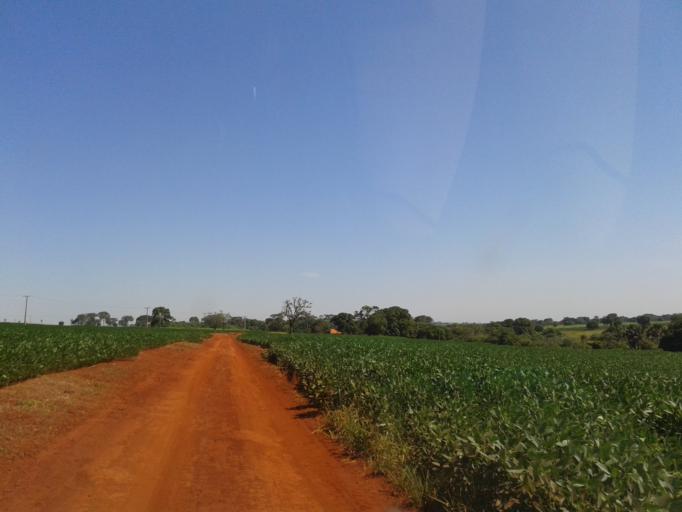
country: BR
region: Minas Gerais
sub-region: Centralina
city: Centralina
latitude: -18.6432
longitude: -49.2973
